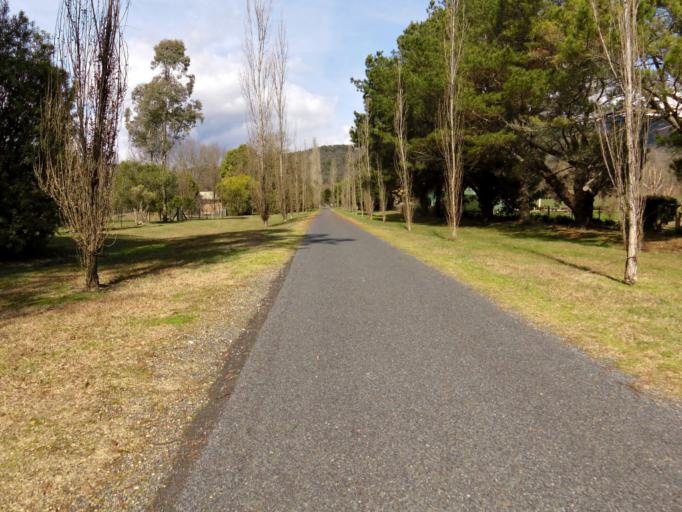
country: AU
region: Victoria
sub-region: Alpine
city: Mount Beauty
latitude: -36.7212
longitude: 146.9453
